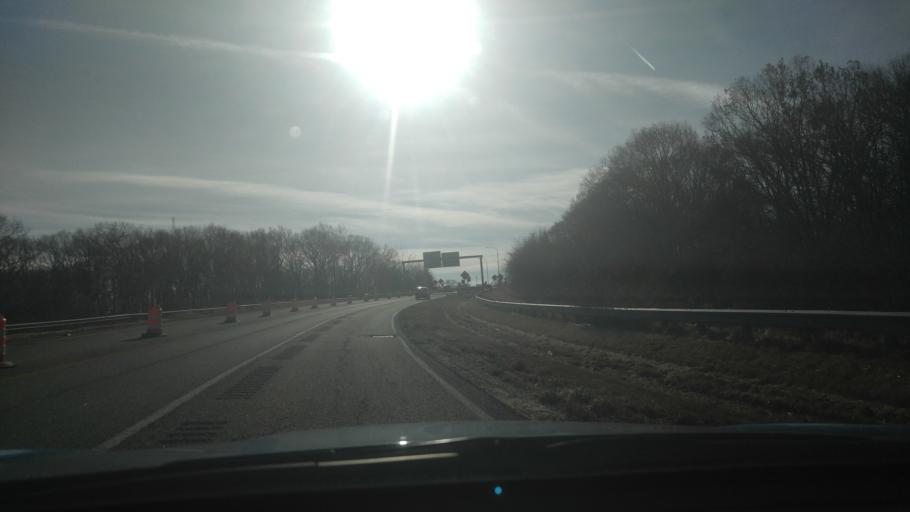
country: US
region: Rhode Island
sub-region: Providence County
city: Cumberland Hill
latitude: 41.9537
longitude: -71.4836
